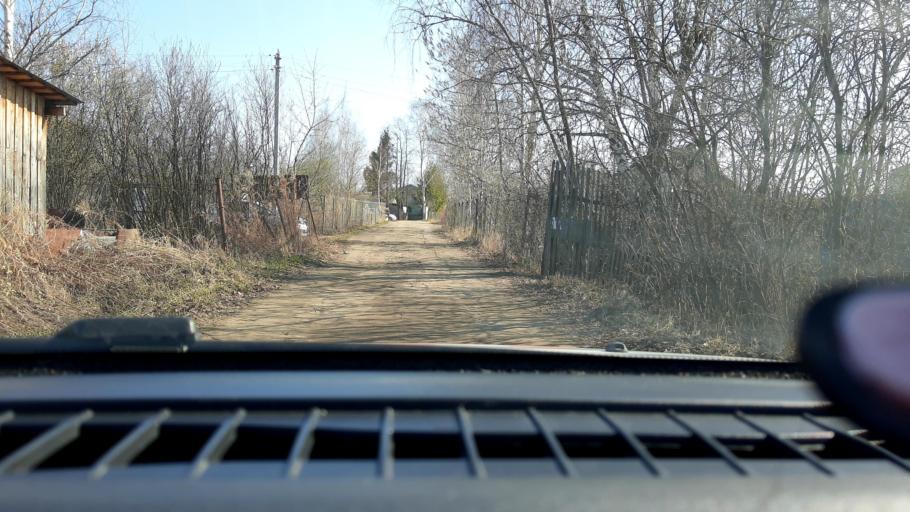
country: RU
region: Nizjnij Novgorod
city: Gorbatovka
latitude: 56.2642
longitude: 43.8225
